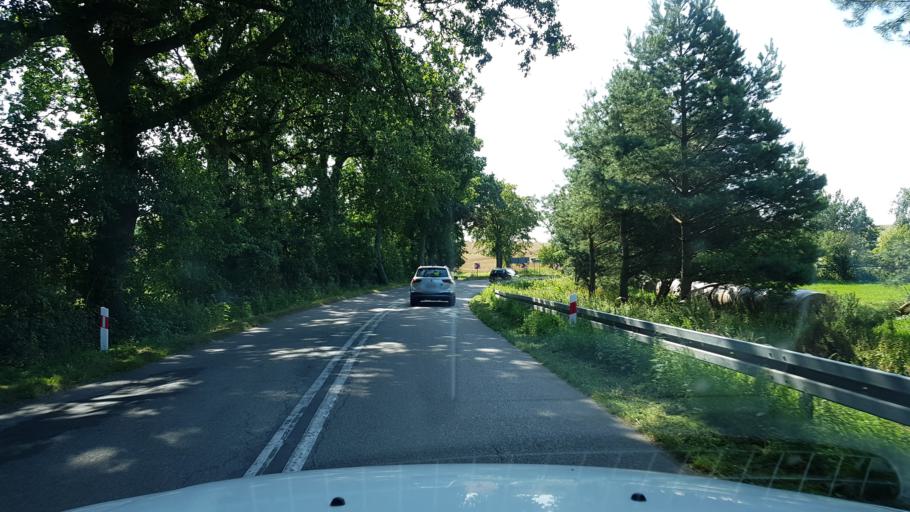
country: PL
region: West Pomeranian Voivodeship
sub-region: Powiat gryficki
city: Cerkwica
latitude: 54.0702
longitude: 15.1182
